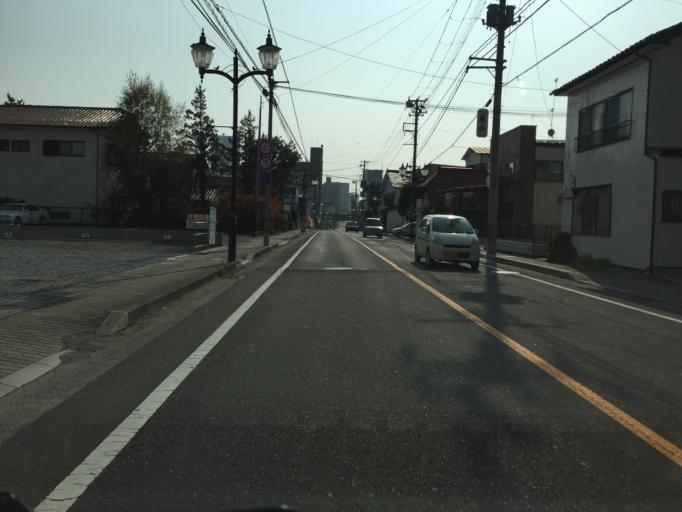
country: JP
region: Fukushima
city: Koriyama
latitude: 37.4085
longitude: 140.3899
